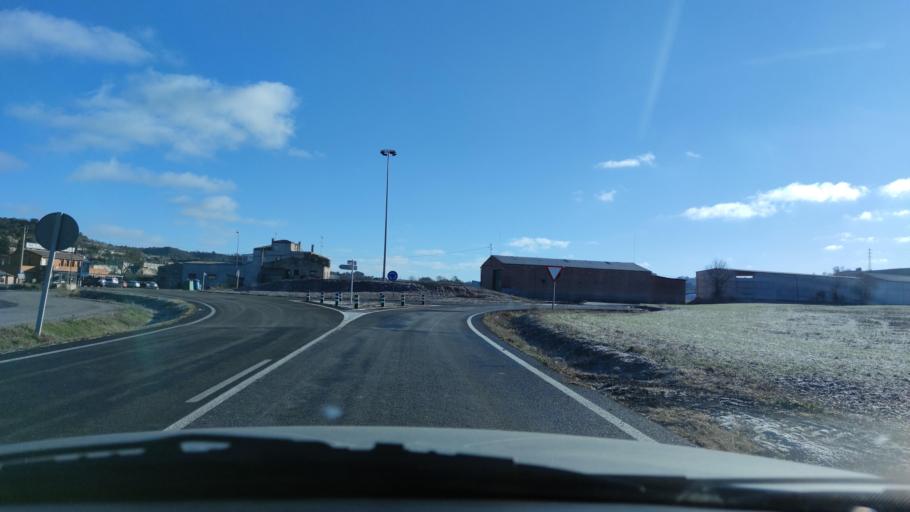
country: ES
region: Catalonia
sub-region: Provincia de Lleida
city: Cervera
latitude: 41.6942
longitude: 1.3189
